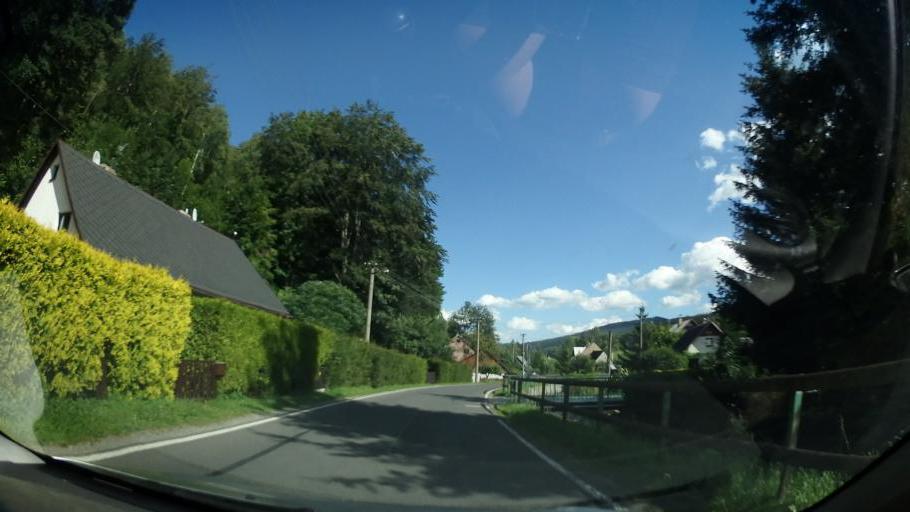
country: CZ
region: Olomoucky
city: Vapenna
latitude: 50.2264
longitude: 17.0850
